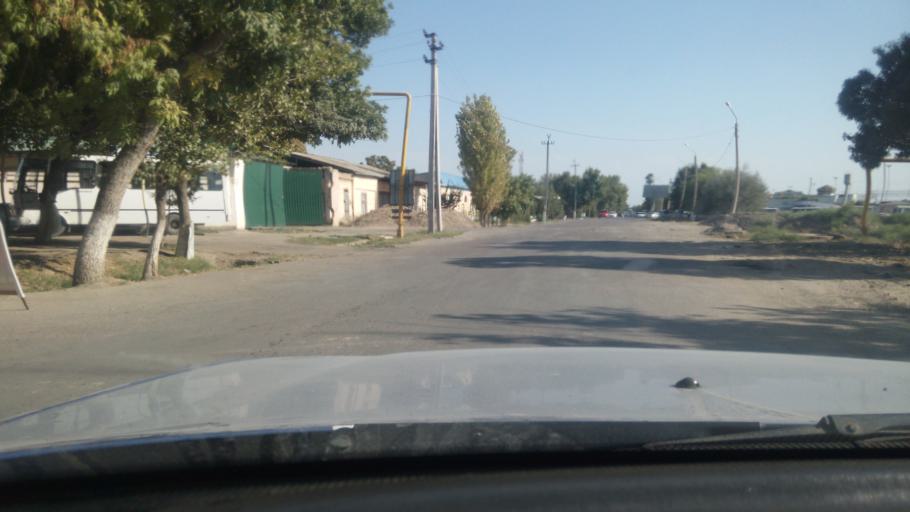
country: UZ
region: Sirdaryo
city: Guliston
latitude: 40.4995
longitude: 68.7651
